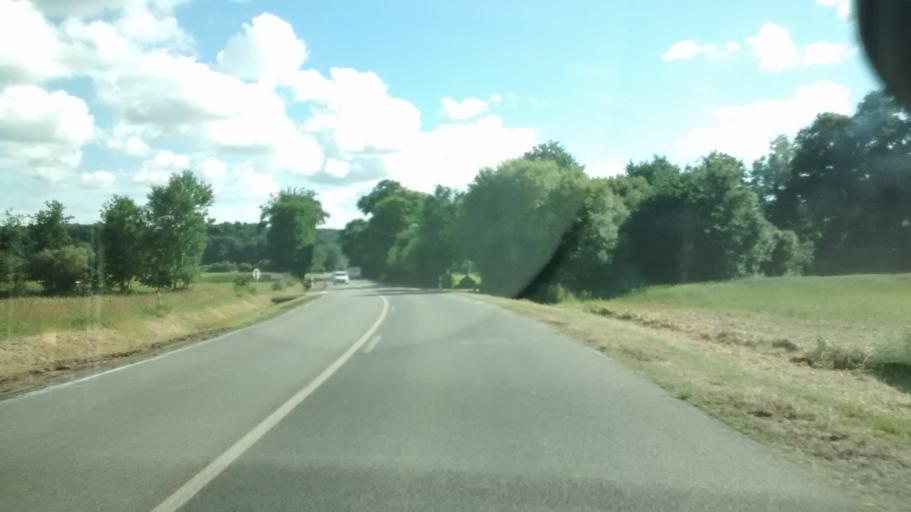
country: FR
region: Brittany
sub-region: Departement du Morbihan
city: Malestroit
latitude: 47.7917
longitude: -2.4215
